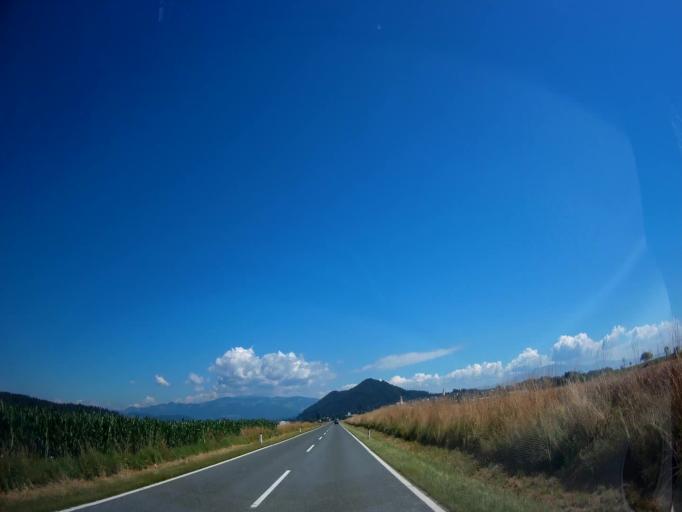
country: AT
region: Carinthia
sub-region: Politischer Bezirk Volkermarkt
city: Eberndorf
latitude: 46.5791
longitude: 14.6312
